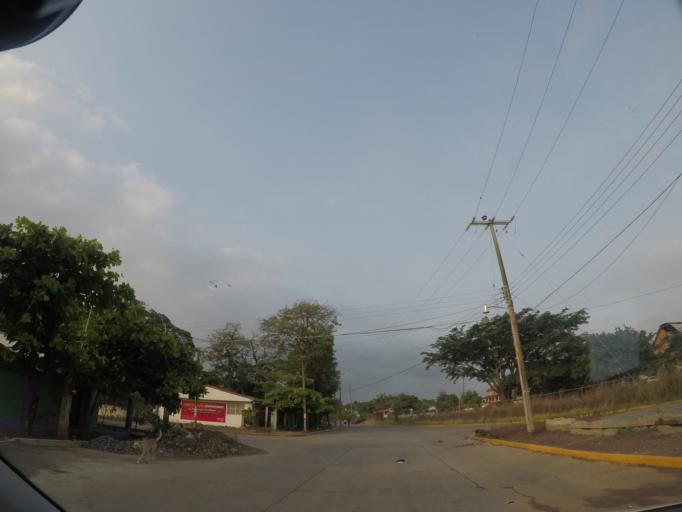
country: MX
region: Oaxaca
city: Matias Romero
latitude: 16.8740
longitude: -95.0447
